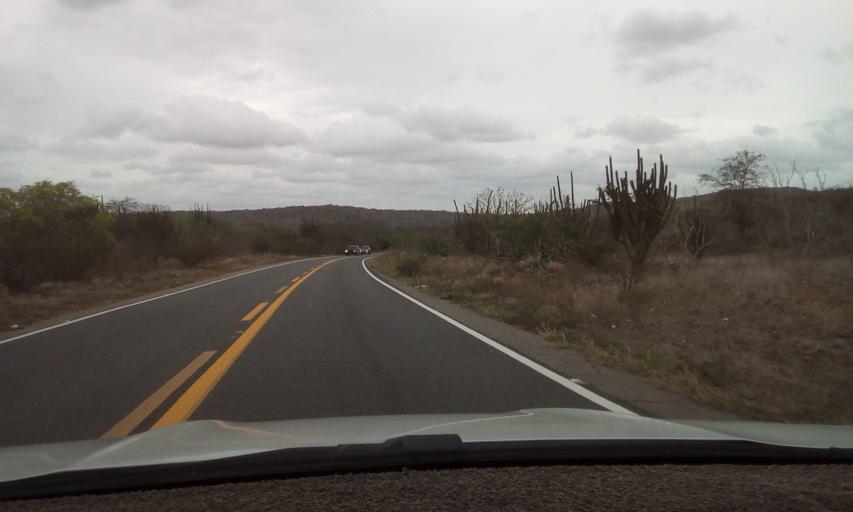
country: BR
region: Paraiba
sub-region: Areia
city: Remigio
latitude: -6.8966
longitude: -35.8949
